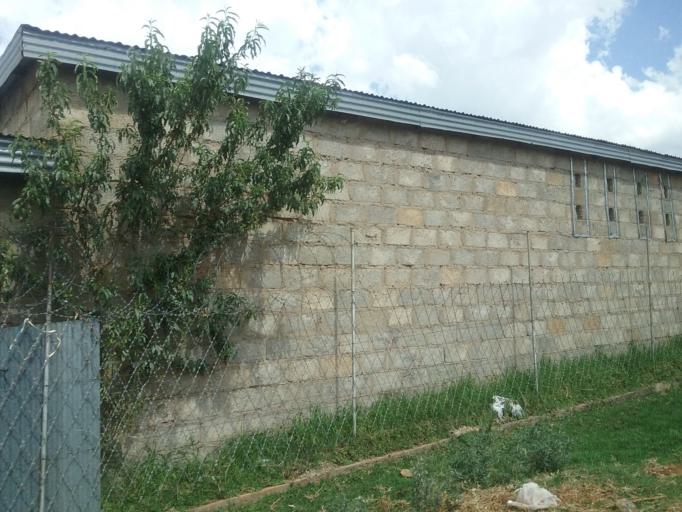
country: LS
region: Maseru
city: Maseru
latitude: -29.4218
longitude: 27.5650
